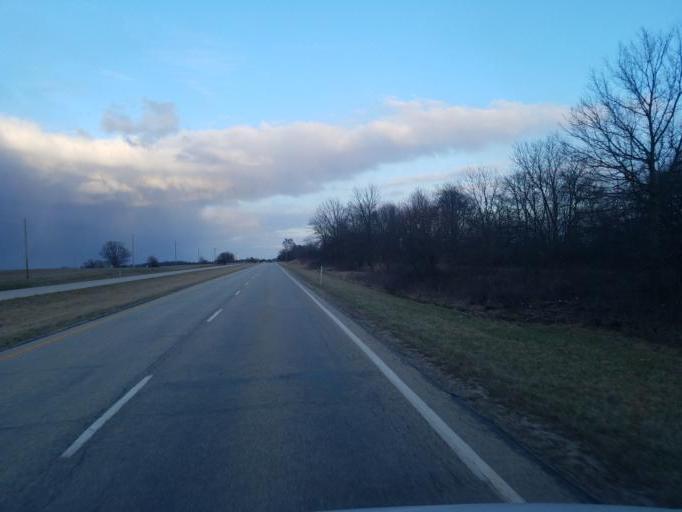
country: US
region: Indiana
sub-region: Henry County
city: Knightstown
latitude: 39.8021
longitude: -85.4662
